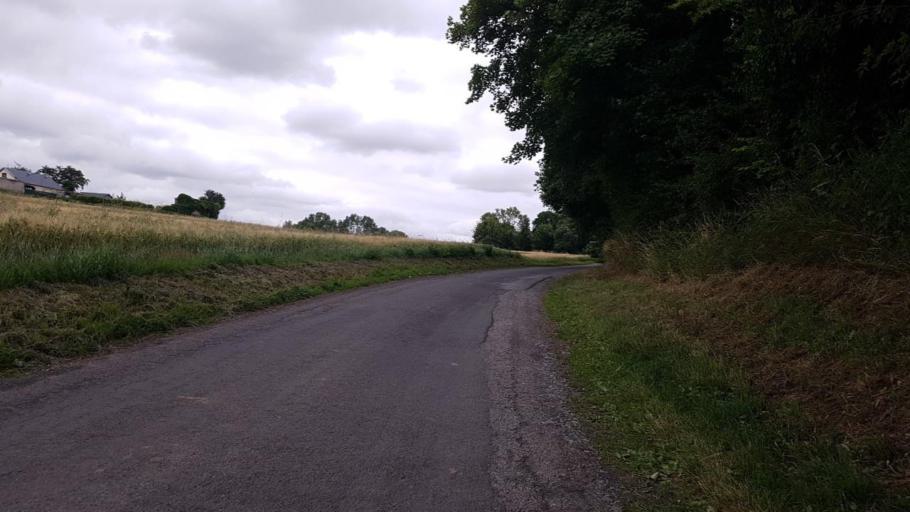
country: FR
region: Picardie
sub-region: Departement de l'Aisne
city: Guise
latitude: 49.8962
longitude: 3.6192
